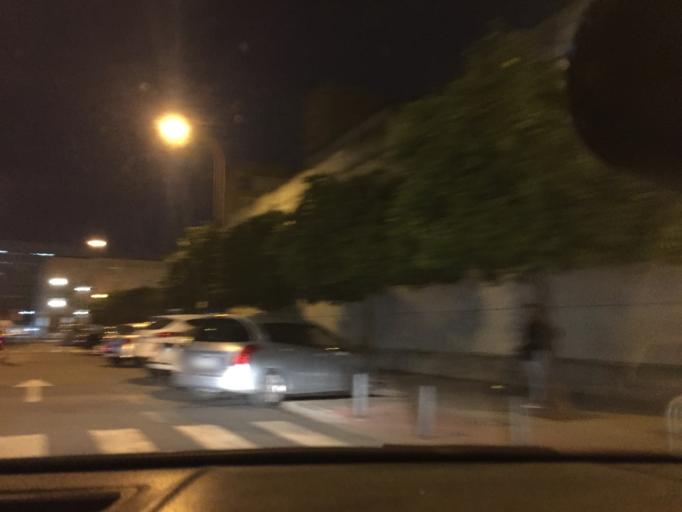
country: ES
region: Andalusia
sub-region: Provincia de Sevilla
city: Sevilla
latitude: 37.3797
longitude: -5.9776
